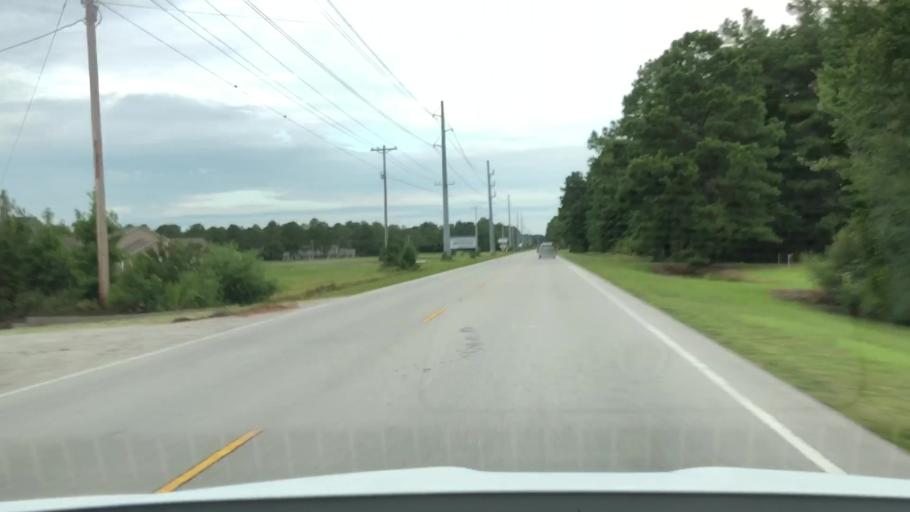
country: US
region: North Carolina
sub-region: Carteret County
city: Cape Carteret
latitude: 34.7367
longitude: -77.0830
